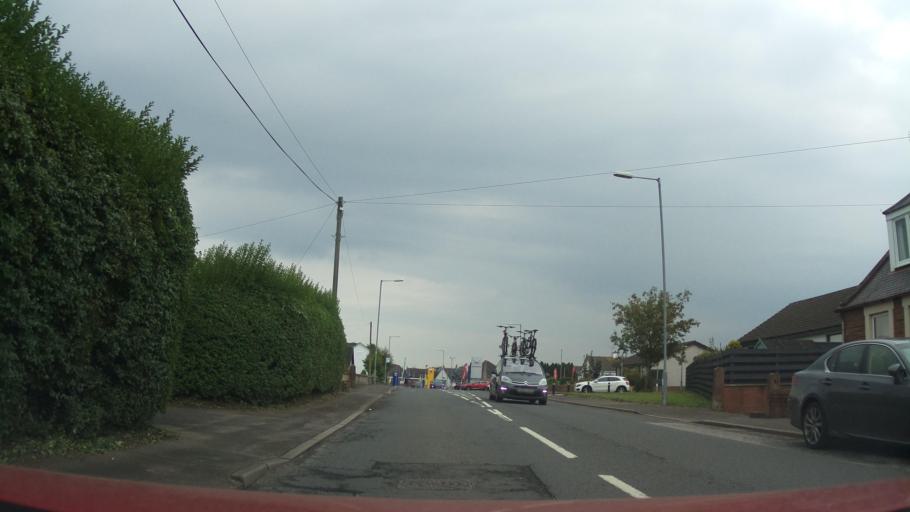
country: GB
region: Scotland
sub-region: Dumfries and Galloway
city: Locharbriggs
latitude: 55.0692
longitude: -3.5695
